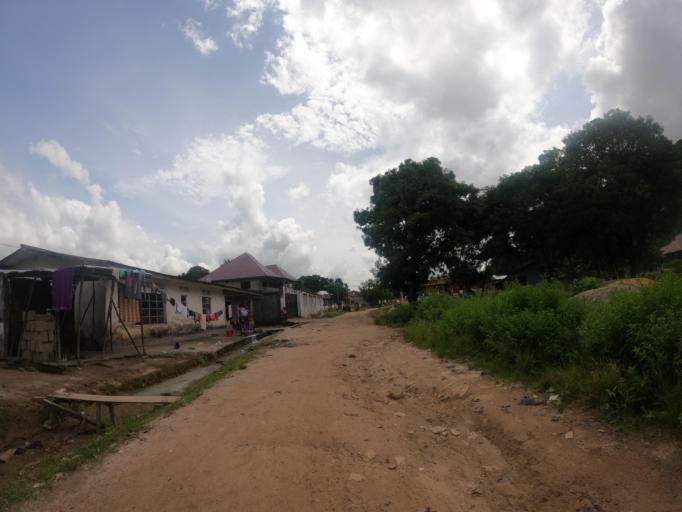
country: SL
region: Northern Province
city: Makeni
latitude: 8.8903
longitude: -12.0644
